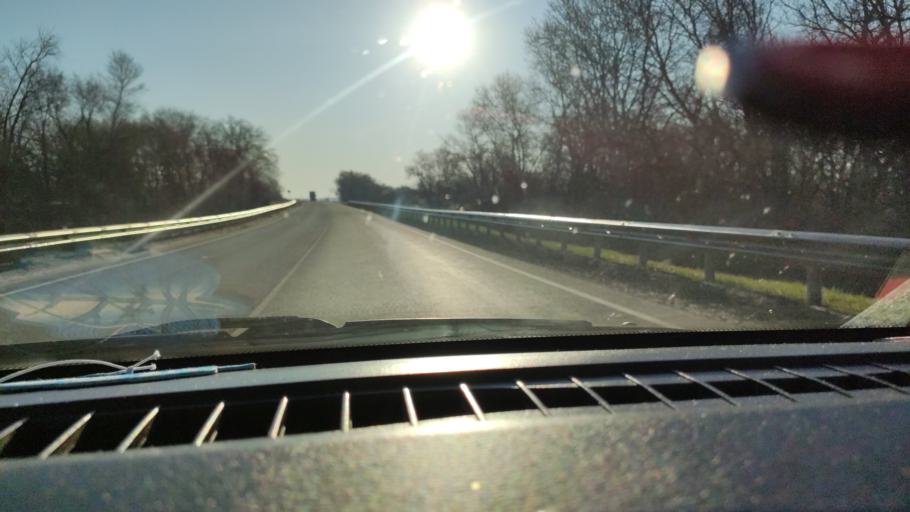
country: RU
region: Saratov
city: Tersa
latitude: 52.0850
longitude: 47.5954
